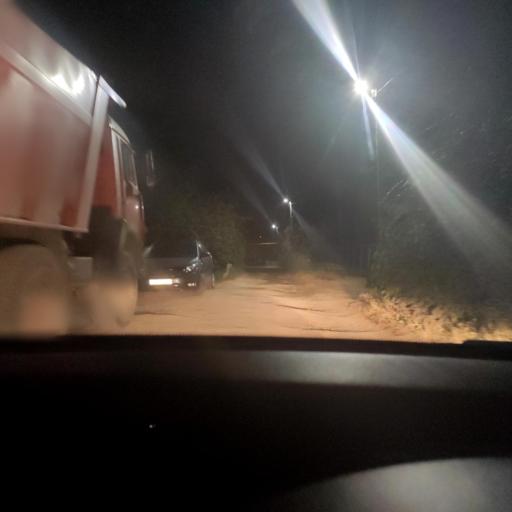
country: RU
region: Samara
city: Samara
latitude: 53.2220
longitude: 50.2230
